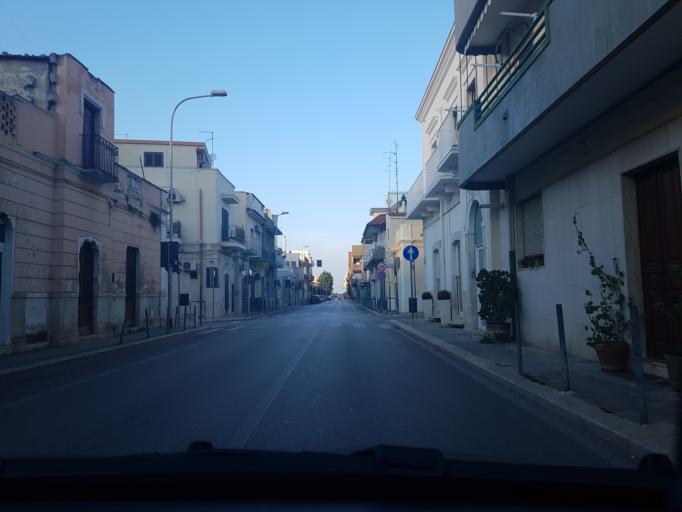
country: IT
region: Apulia
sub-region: Provincia di Bari
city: Bitritto
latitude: 41.0440
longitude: 16.8268
